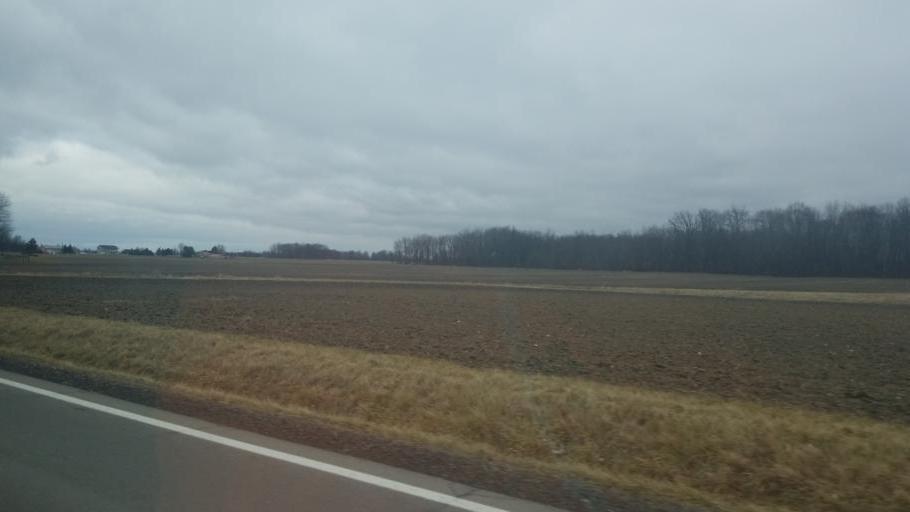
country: US
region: Ohio
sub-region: Crawford County
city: Crestline
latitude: 40.8196
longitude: -82.7302
